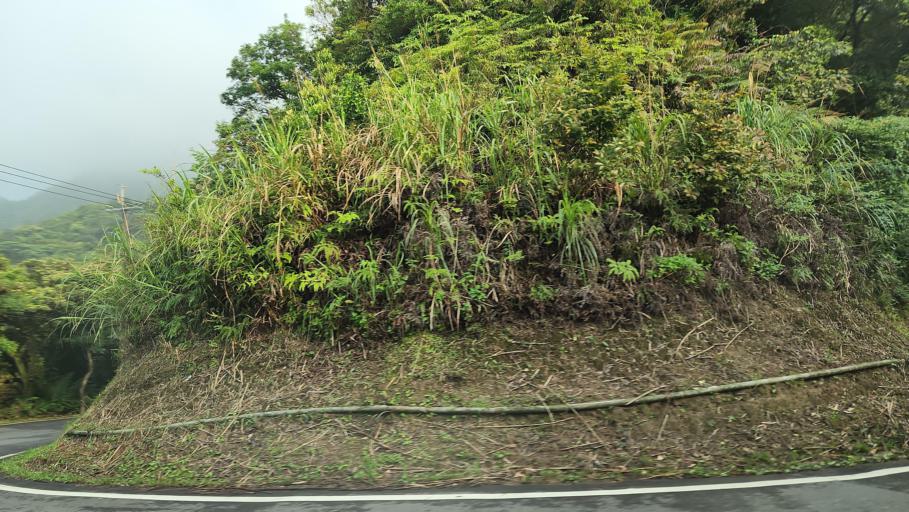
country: TW
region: Taiwan
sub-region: Keelung
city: Keelung
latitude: 25.1496
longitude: 121.6247
